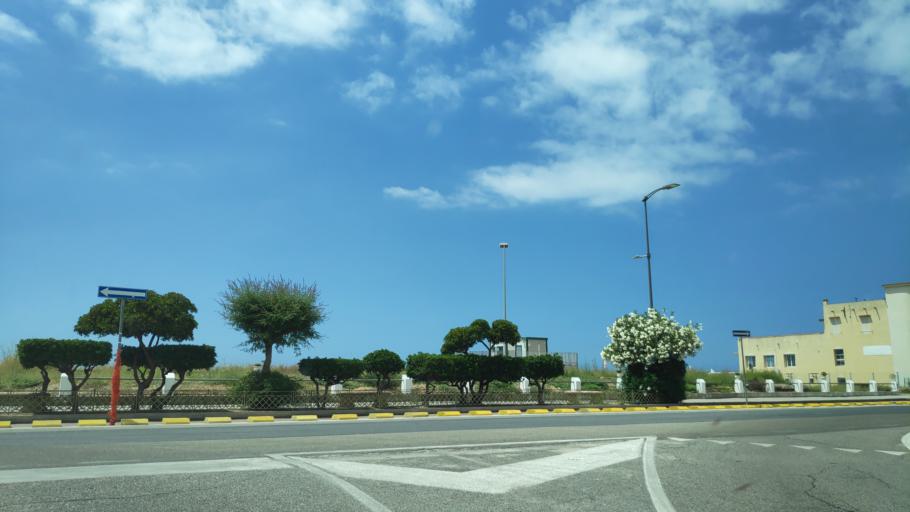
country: IT
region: Calabria
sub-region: Provincia di Cosenza
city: Paola
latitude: 39.3577
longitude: 16.0323
